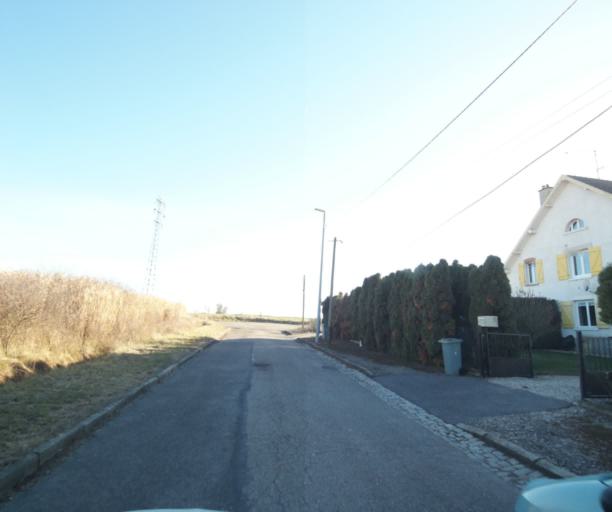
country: FR
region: Lorraine
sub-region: Departement de Meurthe-et-Moselle
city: Art-sur-Meurthe
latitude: 48.6355
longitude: 6.2705
